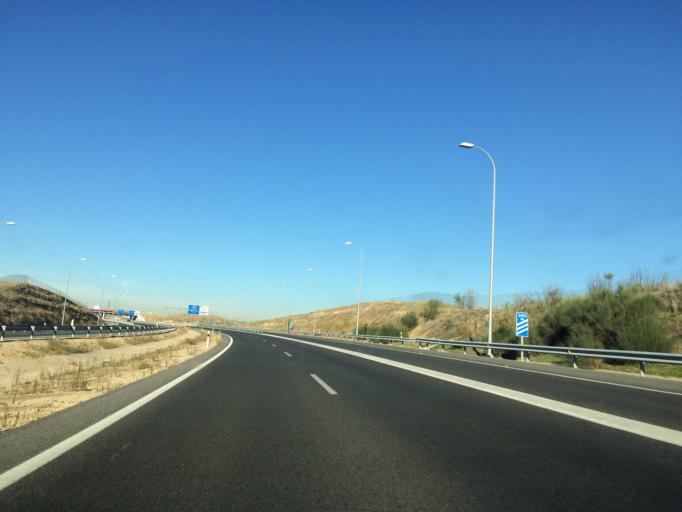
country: ES
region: Madrid
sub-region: Provincia de Madrid
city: Moraleja de Enmedio
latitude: 40.2386
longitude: -3.8572
